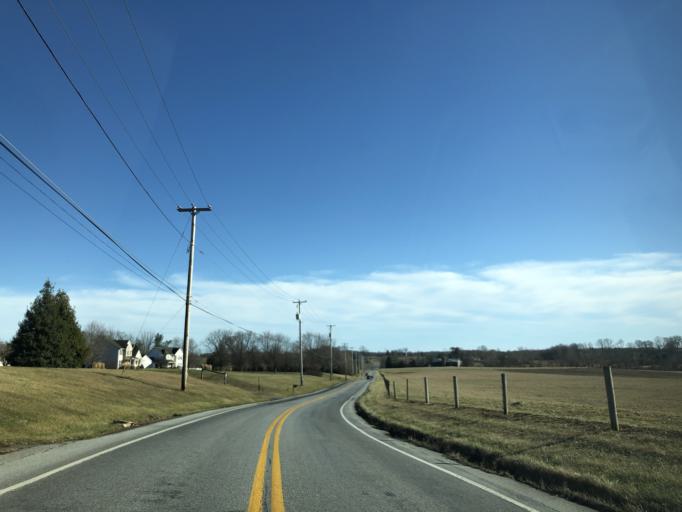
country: US
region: Pennsylvania
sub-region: Chester County
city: Oxford
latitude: 39.7413
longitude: -76.0007
